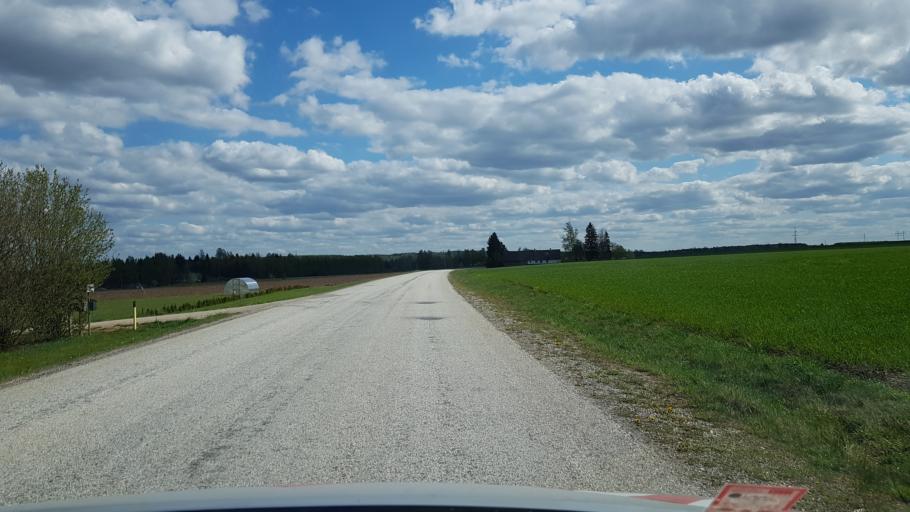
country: EE
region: Tartu
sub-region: UElenurme vald
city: Ulenurme
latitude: 58.2854
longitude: 26.9007
